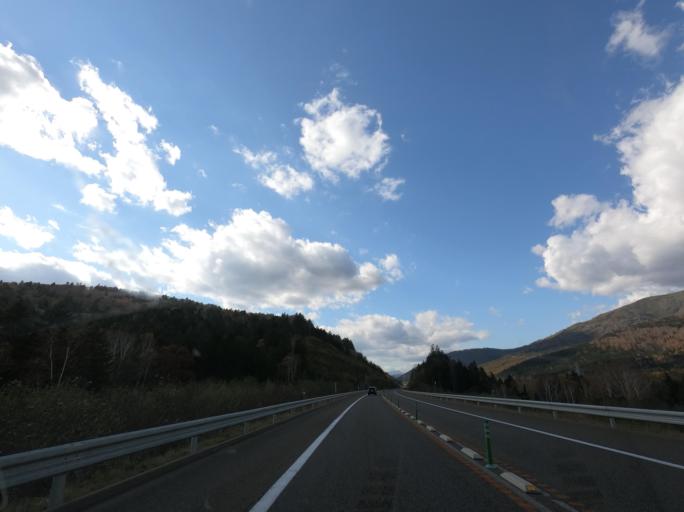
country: JP
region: Hokkaido
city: Shimo-furano
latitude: 43.0517
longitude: 142.6250
